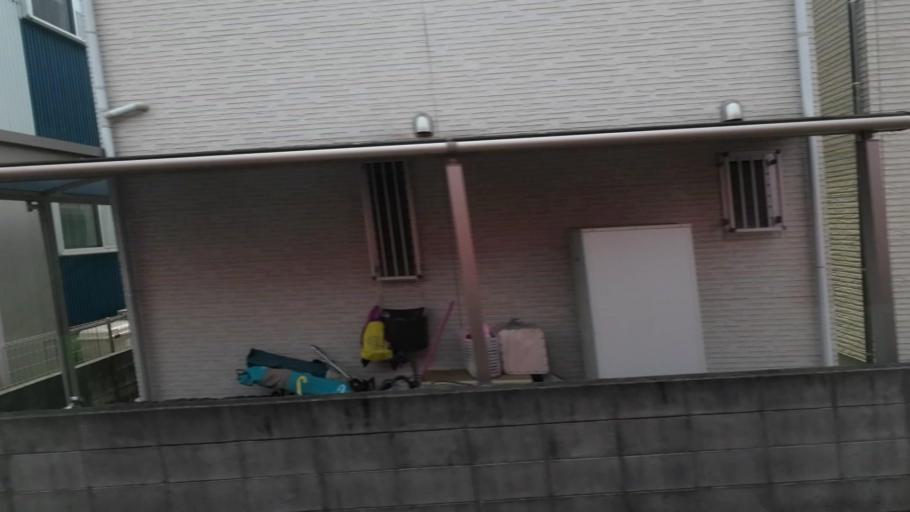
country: JP
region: Kochi
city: Kochi-shi
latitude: 33.6055
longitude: 133.6790
